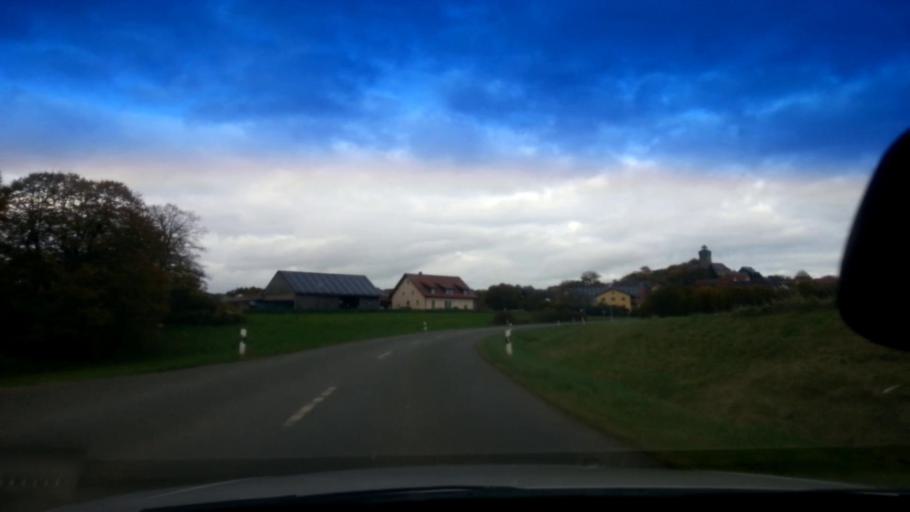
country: DE
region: Bavaria
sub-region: Upper Franconia
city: Wonsees
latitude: 49.9816
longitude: 11.3083
